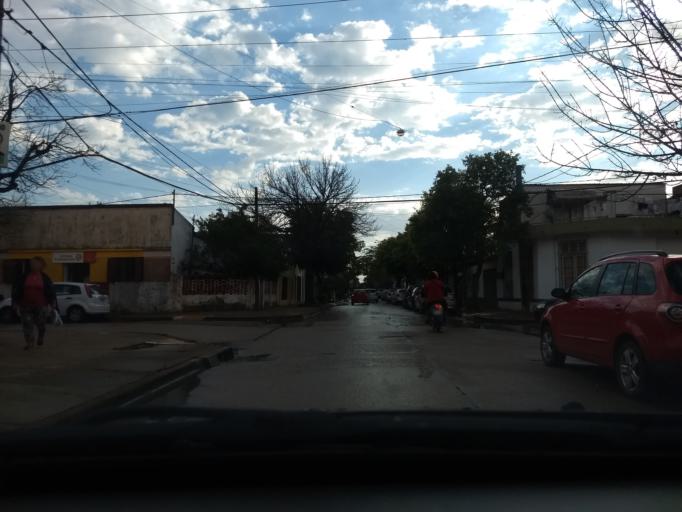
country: AR
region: Corrientes
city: Corrientes
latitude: -27.4752
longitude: -58.8286
